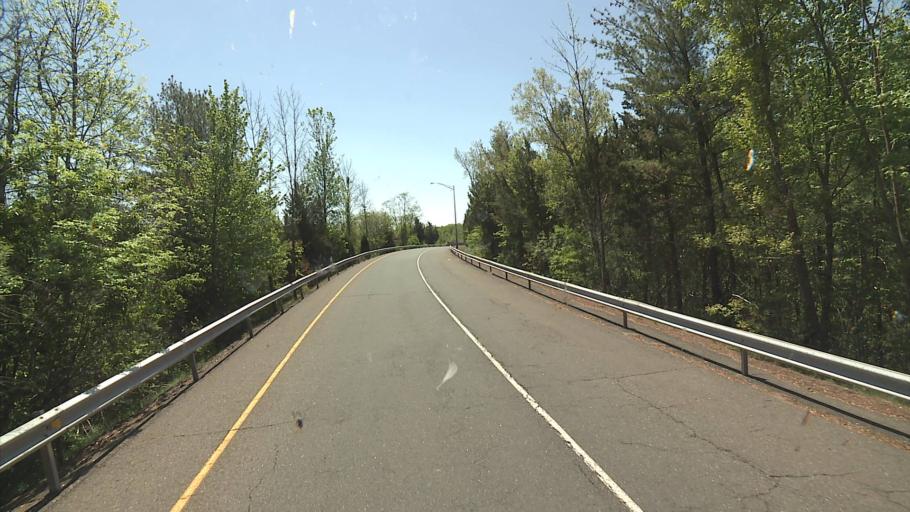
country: US
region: Connecticut
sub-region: Hartford County
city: Farmington
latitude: 41.7213
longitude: -72.7962
